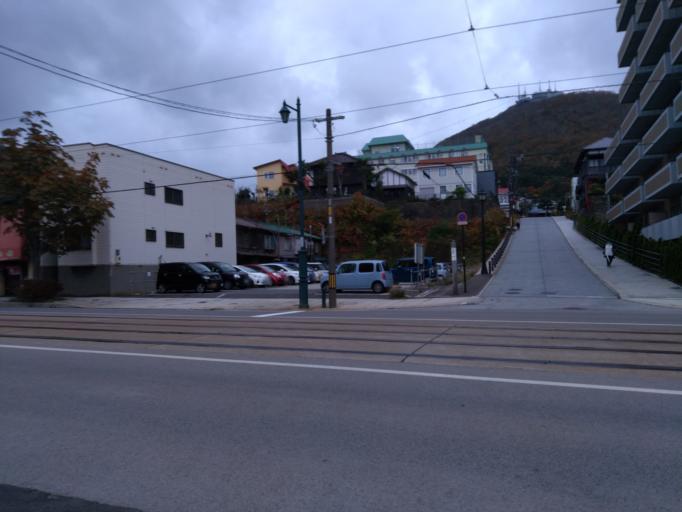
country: JP
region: Hokkaido
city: Hakodate
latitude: 41.7666
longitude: 140.7127
